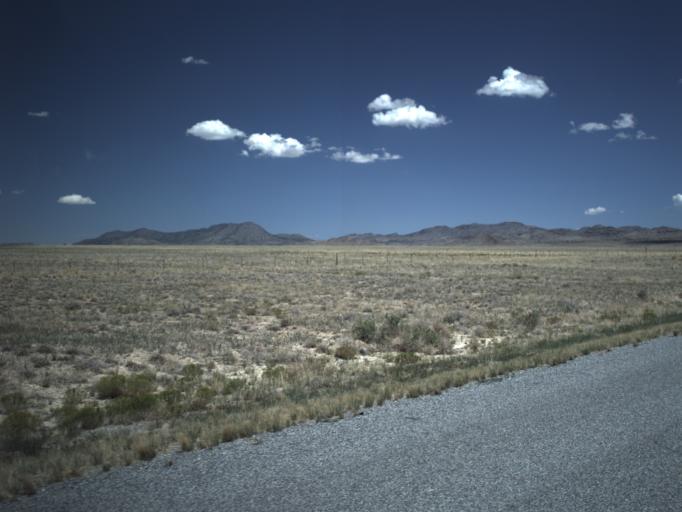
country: US
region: Utah
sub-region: Beaver County
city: Milford
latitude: 39.0485
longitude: -113.7896
